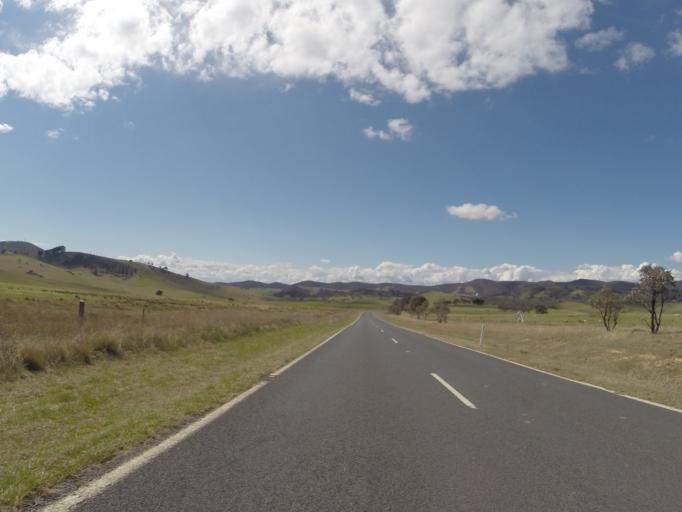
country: AU
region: Australian Capital Territory
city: Macarthur
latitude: -35.4093
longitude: 148.9485
